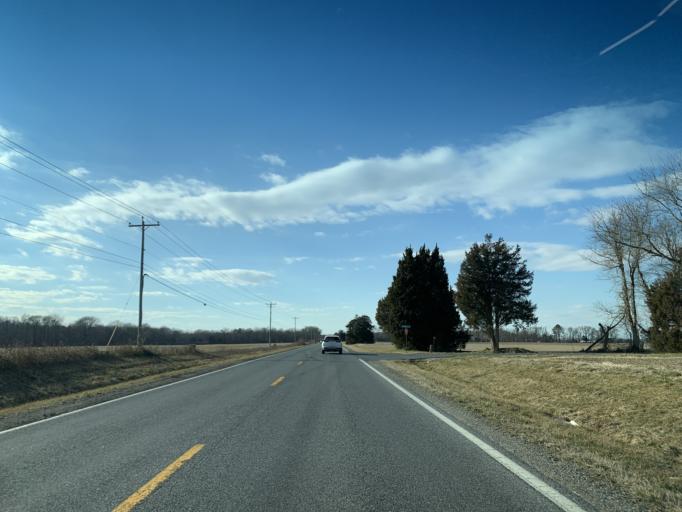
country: US
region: Maryland
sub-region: Queen Anne's County
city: Centreville
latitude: 39.0206
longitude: -76.0095
